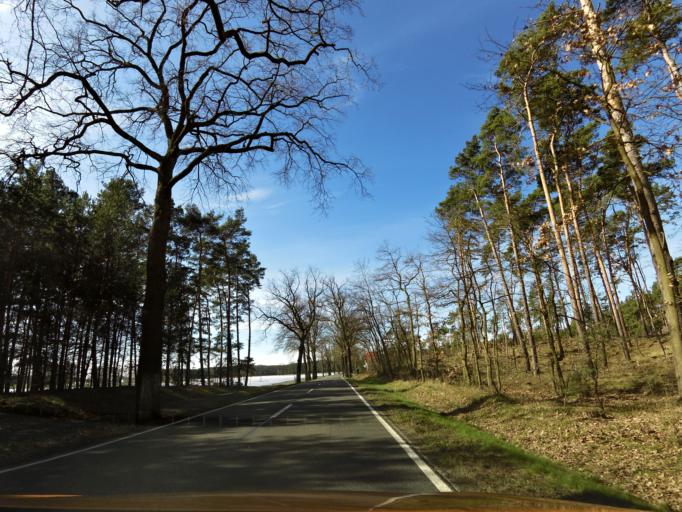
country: DE
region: Brandenburg
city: Beelitz
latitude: 52.2323
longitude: 12.9302
